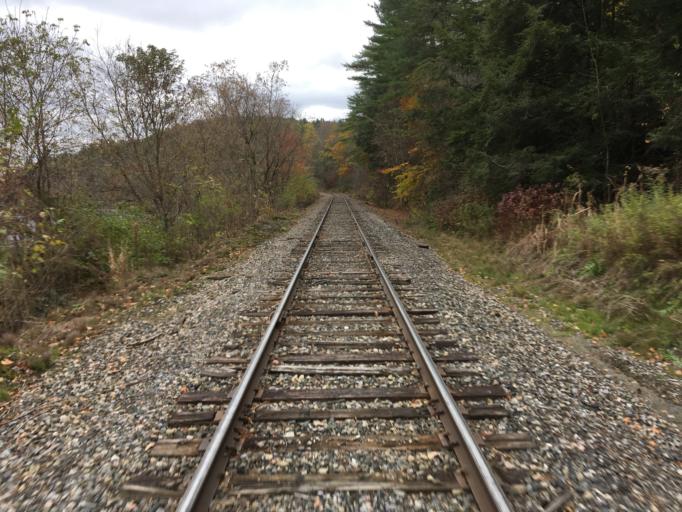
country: US
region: New Hampshire
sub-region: Grafton County
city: Woodsville
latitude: 44.1921
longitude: -72.0663
